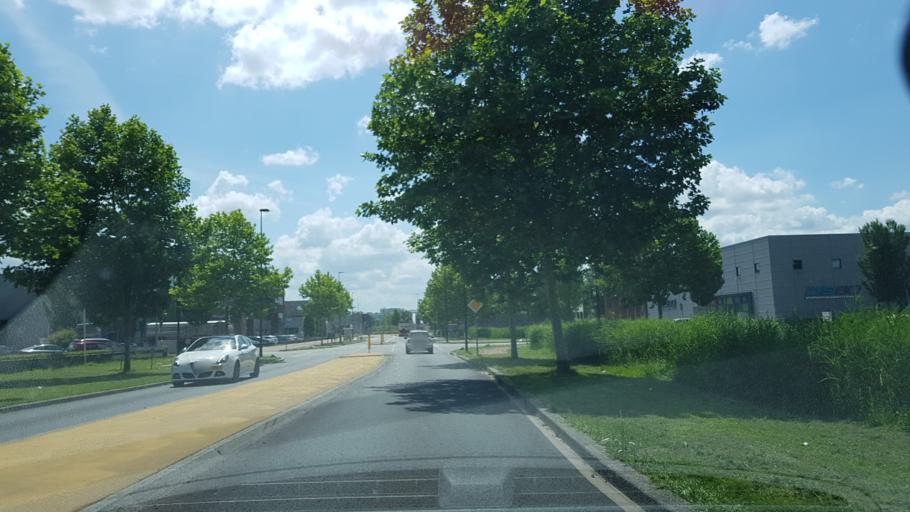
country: NL
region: Utrecht
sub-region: Gemeente Veenendaal
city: Veenendaal
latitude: 52.0455
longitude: 5.5655
